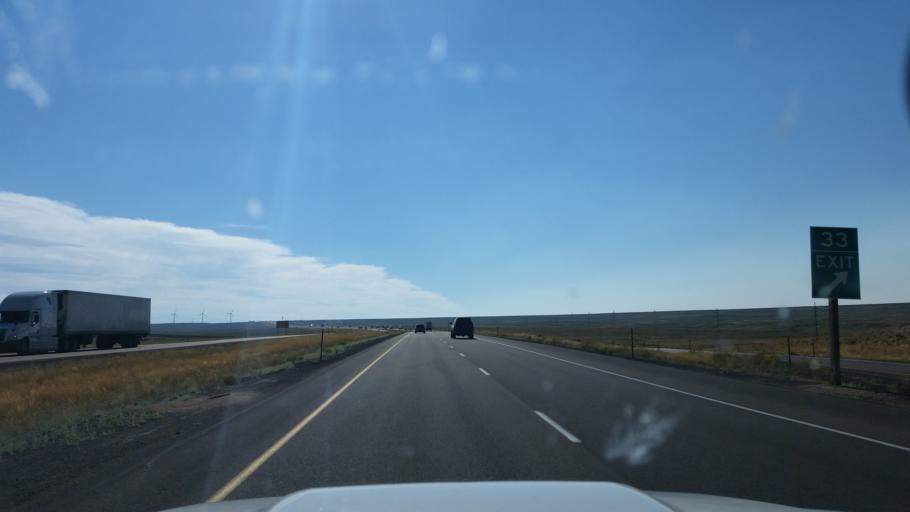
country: US
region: Wyoming
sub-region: Uinta County
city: Mountain View
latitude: 41.3282
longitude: -110.4553
